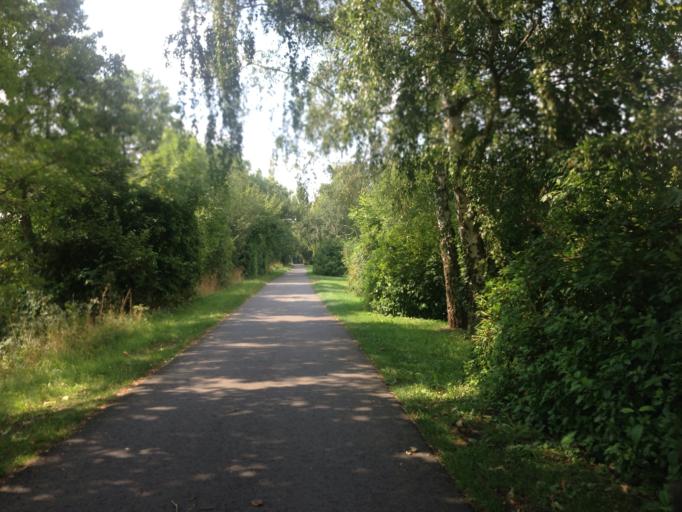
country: DE
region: Hesse
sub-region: Regierungsbezirk Darmstadt
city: Eschborn
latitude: 50.1436
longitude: 8.6201
